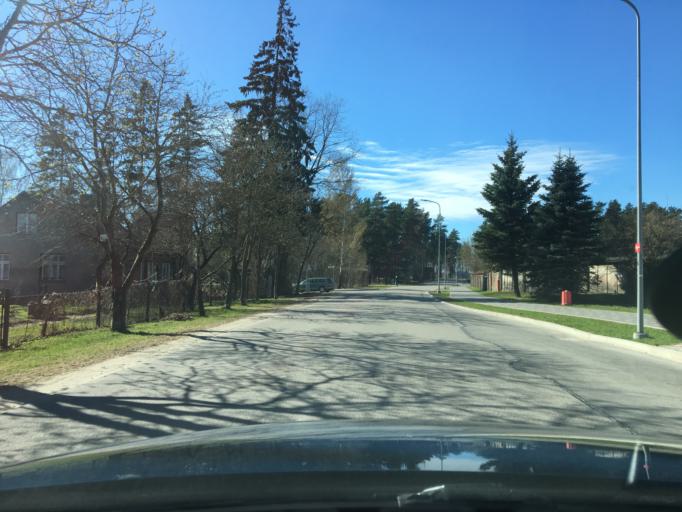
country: LV
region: Salaspils
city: Salaspils
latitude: 56.8698
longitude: 24.3475
